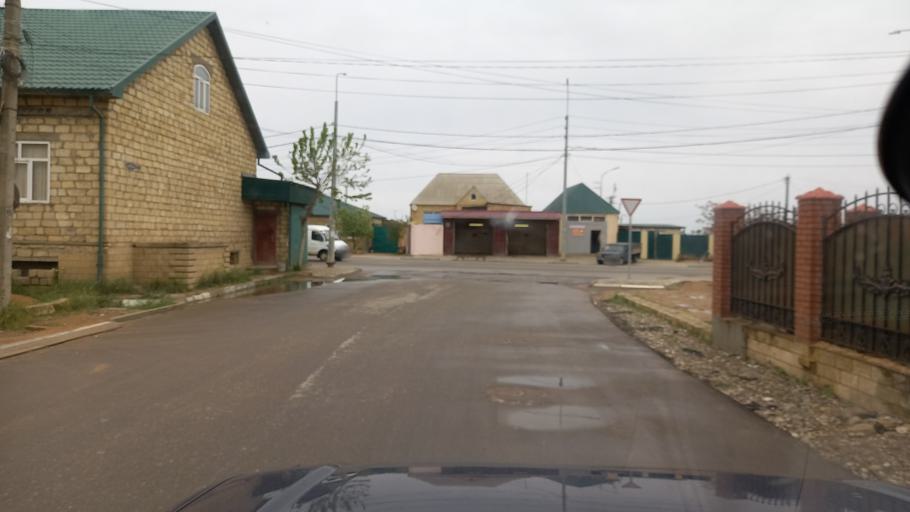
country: RU
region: Dagestan
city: Derbent
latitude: 42.0826
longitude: 48.2934
